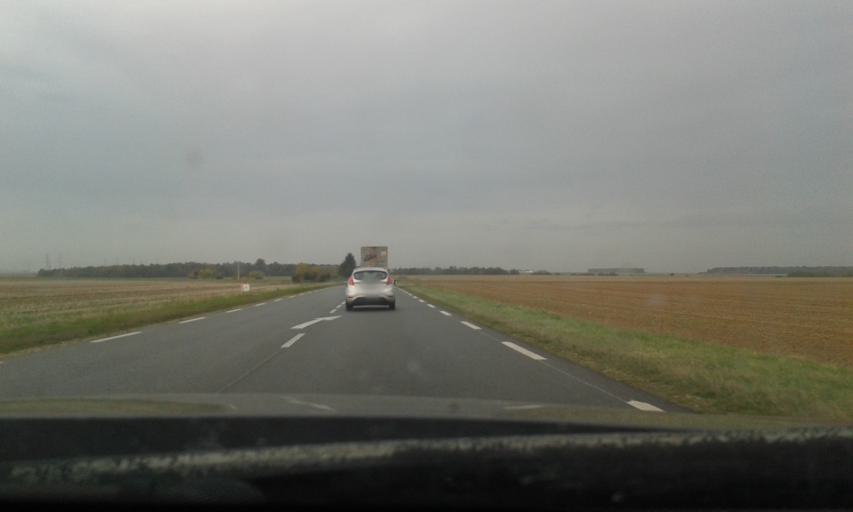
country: FR
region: Centre
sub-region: Departement d'Eure-et-Loir
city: Janville
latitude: 48.2204
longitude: 1.8049
